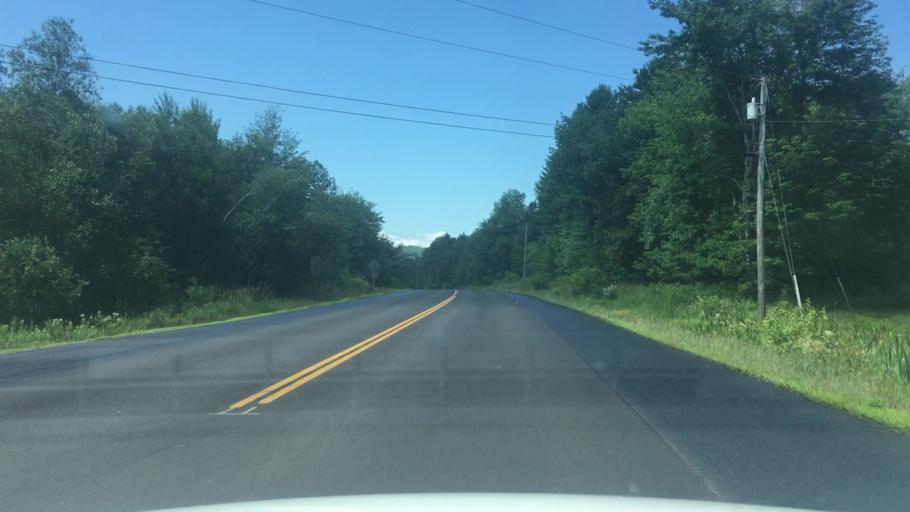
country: US
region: Maine
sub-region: Waldo County
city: Searsmont
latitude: 44.4024
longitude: -69.2704
